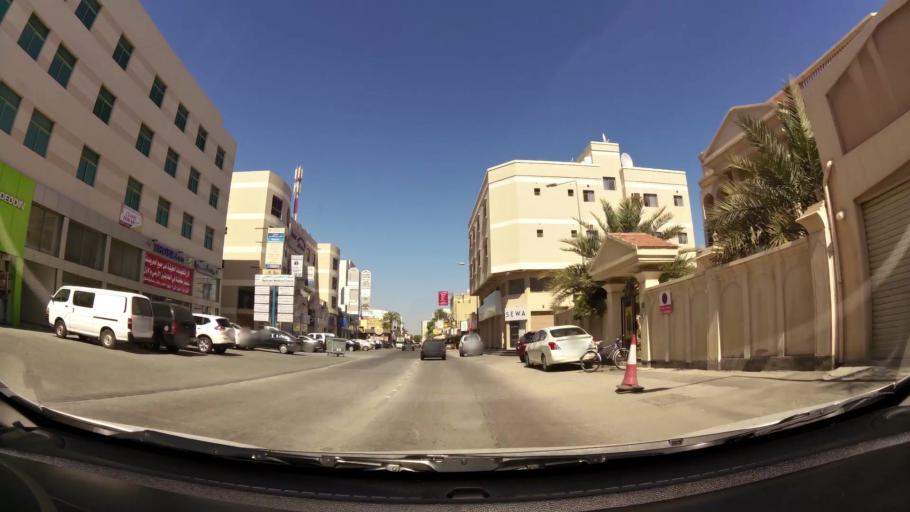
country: BH
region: Muharraq
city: Al Muharraq
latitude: 26.2610
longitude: 50.6190
